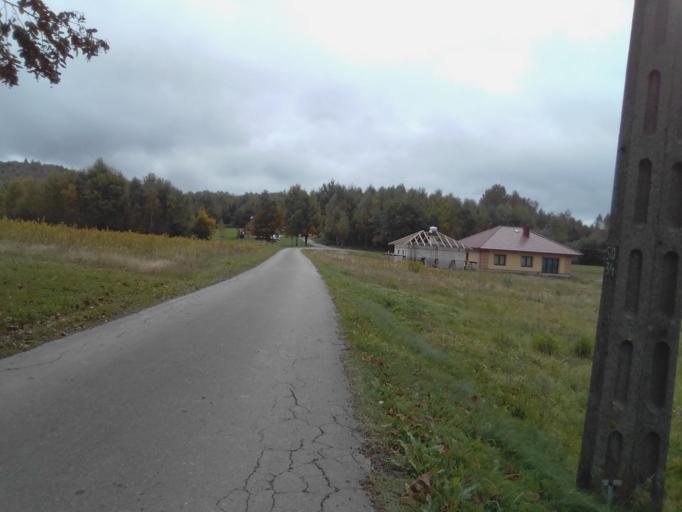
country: PL
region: Subcarpathian Voivodeship
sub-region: Powiat strzyzowski
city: Gwoznica Gorna
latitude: 49.8379
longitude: 22.0068
